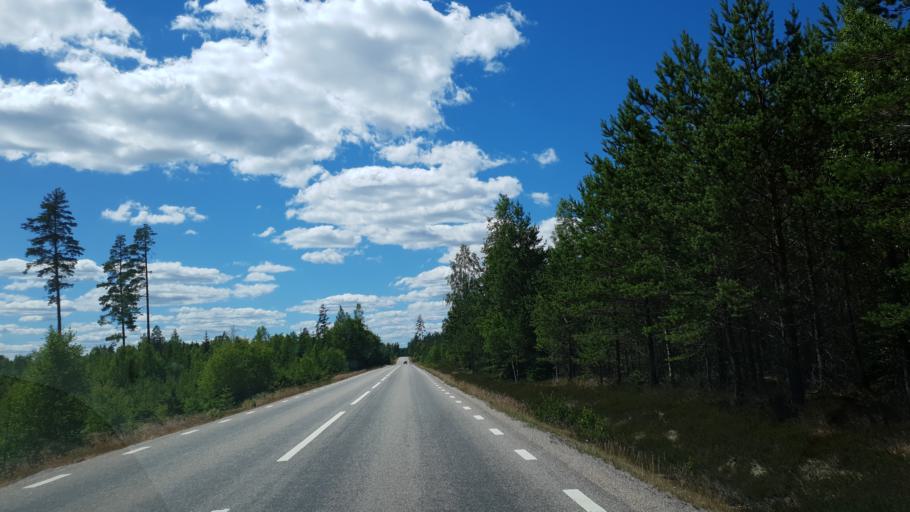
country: SE
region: Kronoberg
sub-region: Lessebo Kommun
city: Lessebo
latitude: 56.8019
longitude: 15.3437
